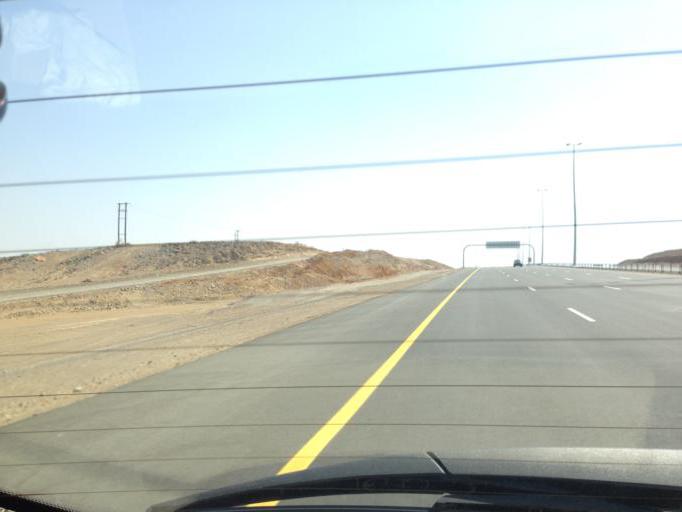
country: OM
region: Al Batinah
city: Rustaq
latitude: 23.5335
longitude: 57.5752
